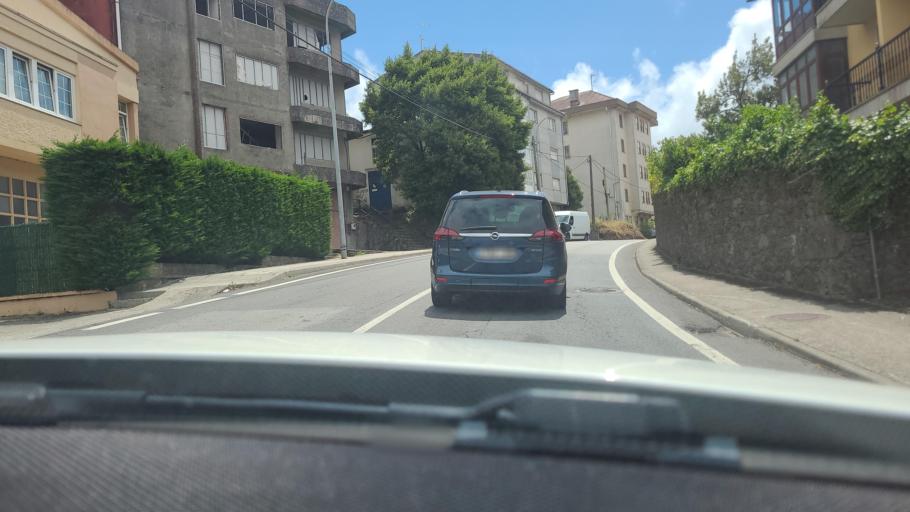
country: ES
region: Galicia
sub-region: Provincia da Coruna
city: Cee
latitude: 42.9545
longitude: -9.1871
